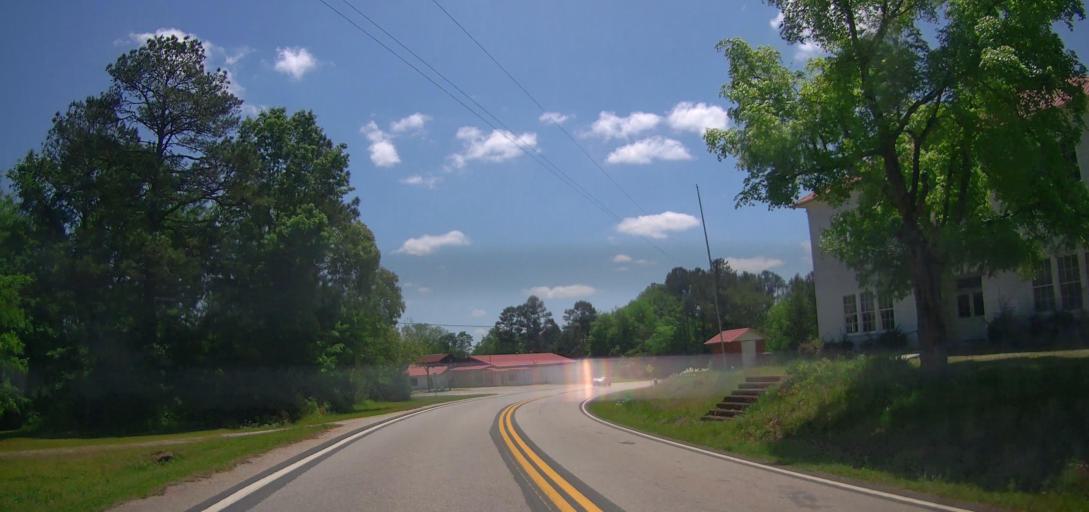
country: US
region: Georgia
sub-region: Jasper County
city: Monticello
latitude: 33.1770
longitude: -83.6390
